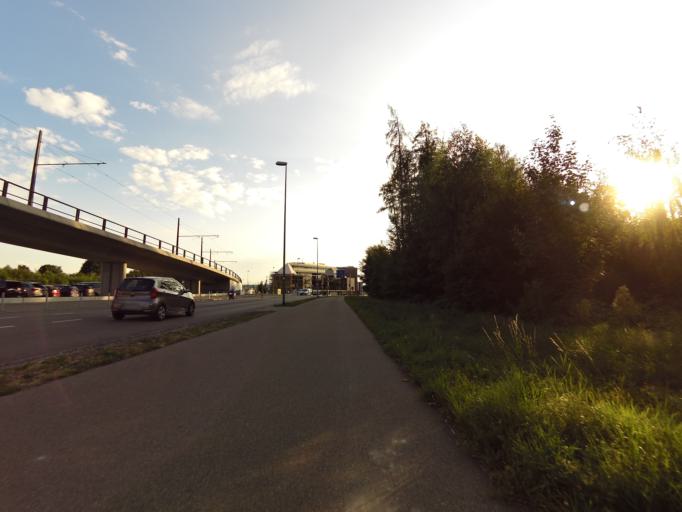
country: CH
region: Zurich
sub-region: Bezirk Buelach
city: Glattbrugg / Rohr/Platten-Balsberg
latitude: 47.4415
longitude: 8.5676
